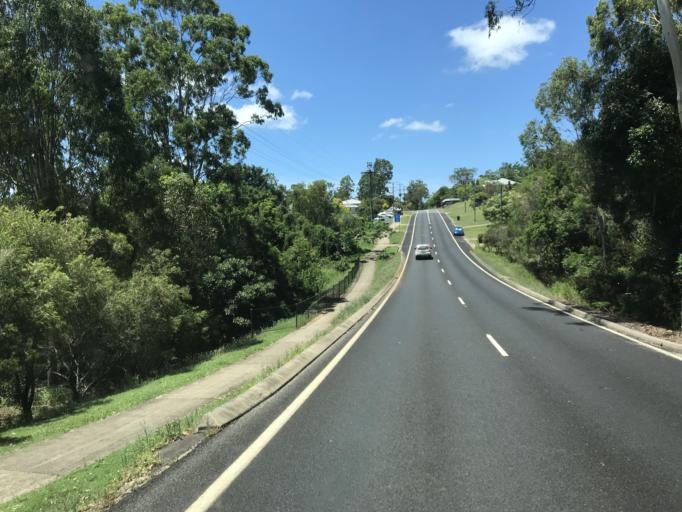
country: AU
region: Queensland
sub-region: Tablelands
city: Atherton
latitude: -17.3888
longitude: 145.3871
